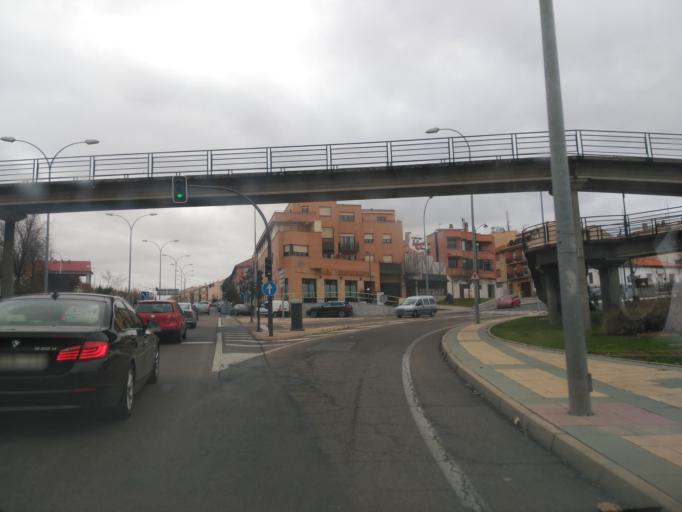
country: ES
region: Castille and Leon
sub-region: Provincia de Salamanca
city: Salamanca
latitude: 40.9528
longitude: -5.6700
